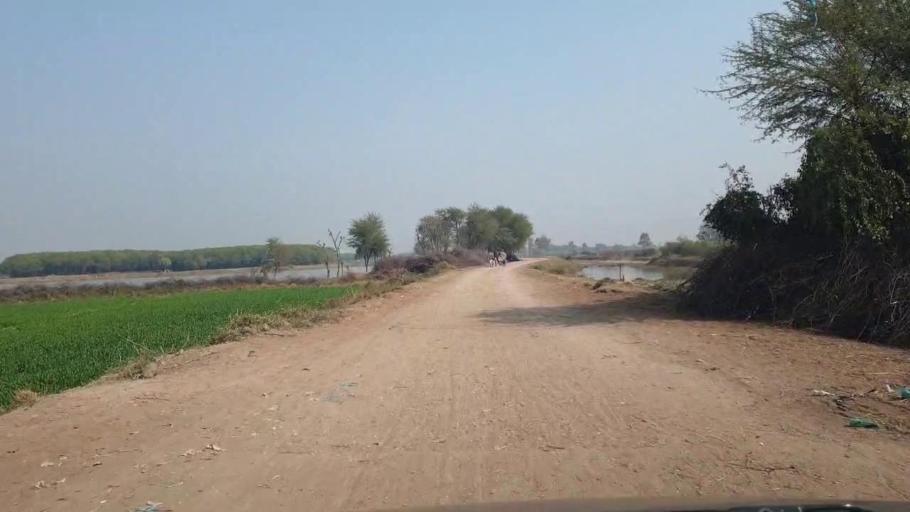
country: PK
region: Sindh
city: Hala
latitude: 25.9638
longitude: 68.4225
